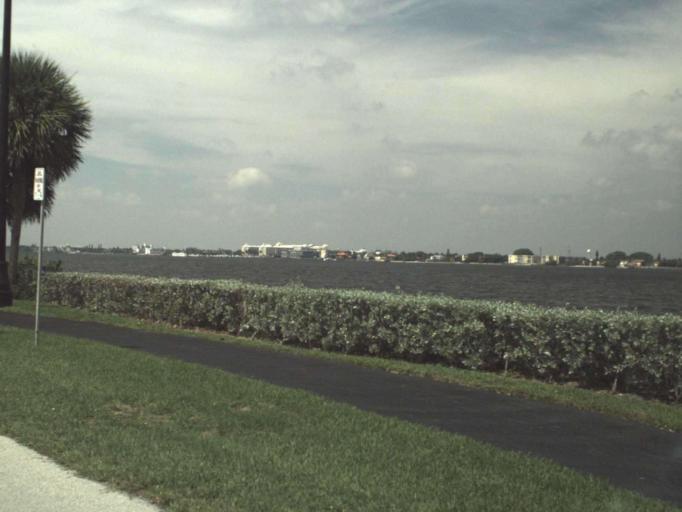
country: US
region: Florida
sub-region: Palm Beach County
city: South Palm Beach
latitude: 26.6048
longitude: -80.0386
